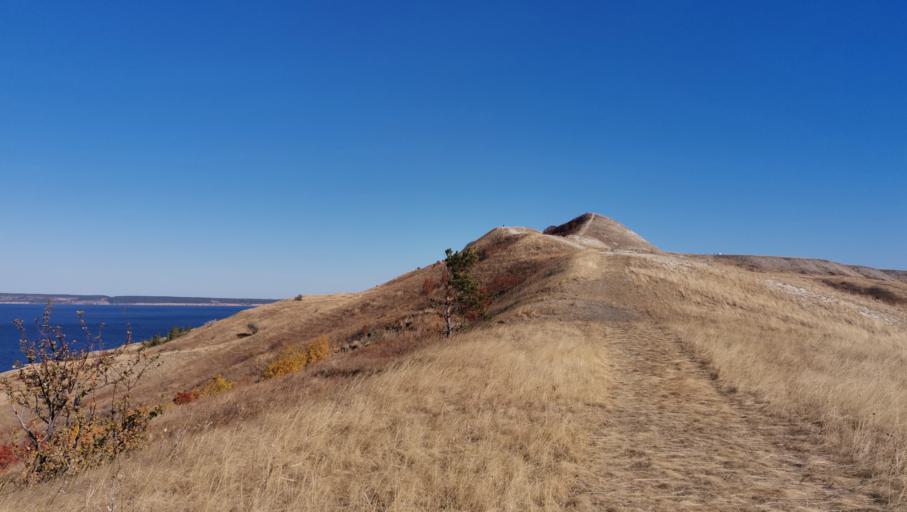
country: RU
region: Ulyanovsk
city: Novoul'yanovsk
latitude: 54.1128
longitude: 48.5630
